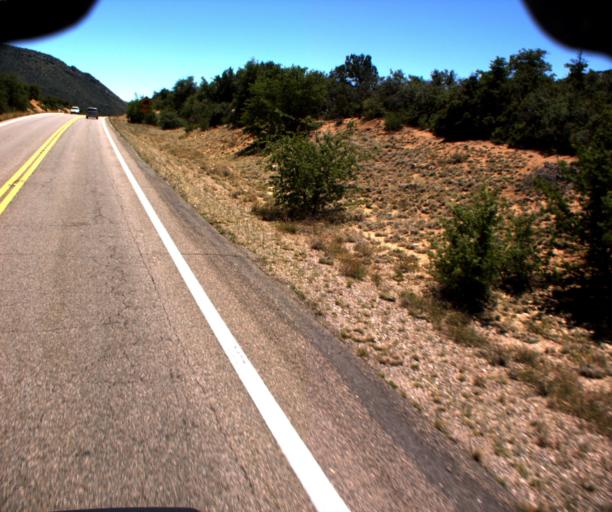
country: US
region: Arizona
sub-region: Gila County
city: Globe
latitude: 33.2433
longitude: -110.7829
